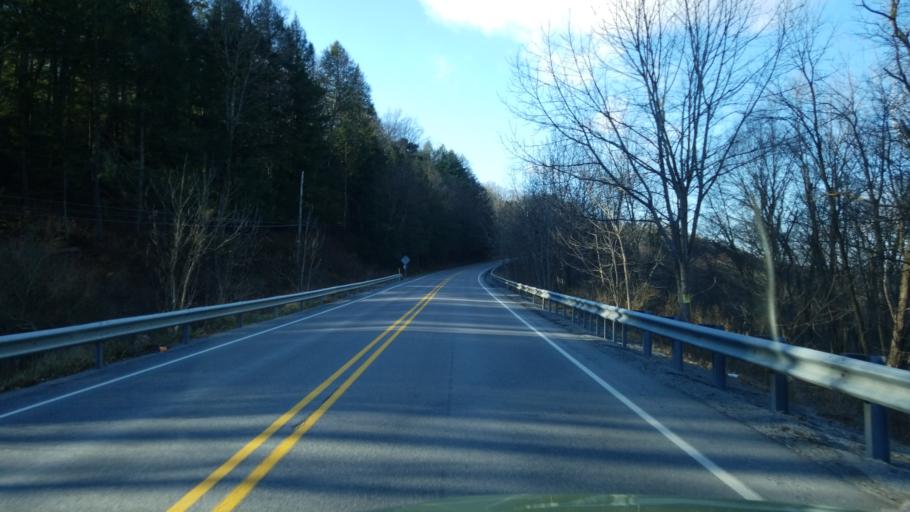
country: US
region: Pennsylvania
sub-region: Clearfield County
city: Clearfield
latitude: 41.0016
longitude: -78.4297
